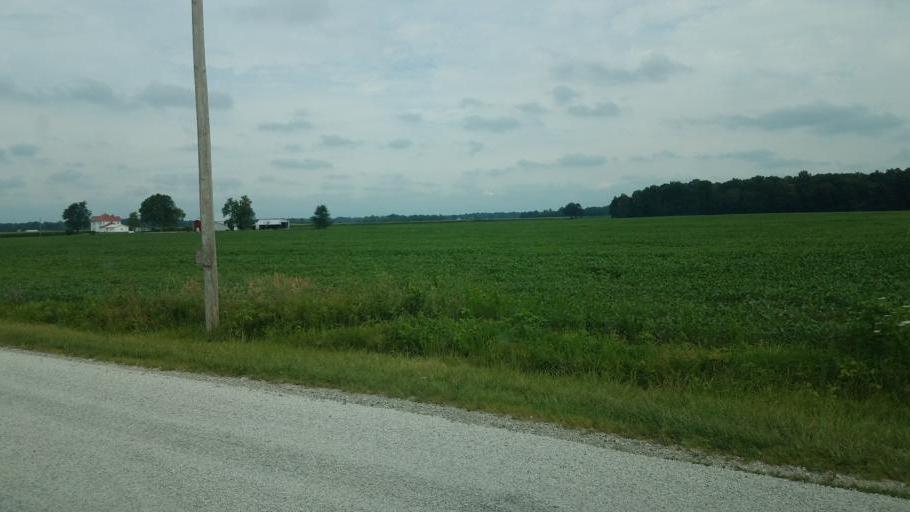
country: US
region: Ohio
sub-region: Morrow County
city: Cardington
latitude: 40.5138
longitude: -82.9817
